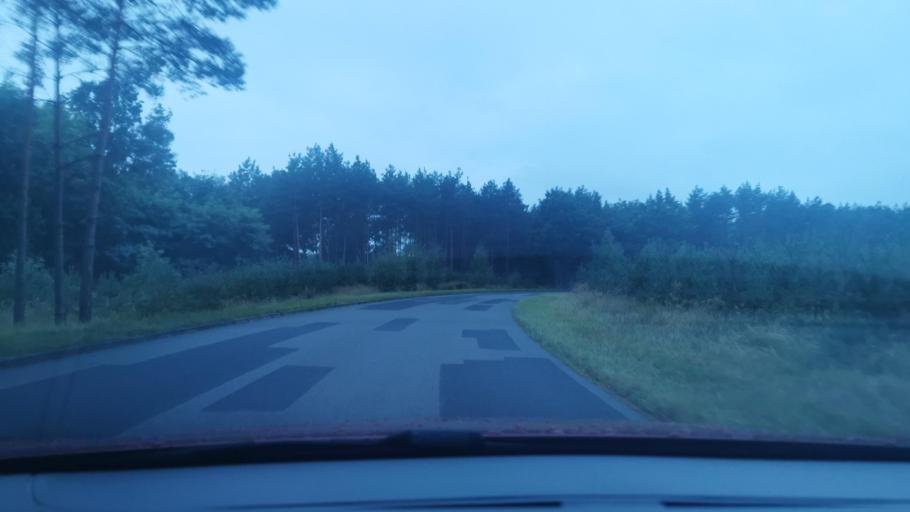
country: DE
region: Brandenburg
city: Kolkwitz
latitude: 51.7276
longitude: 14.2276
